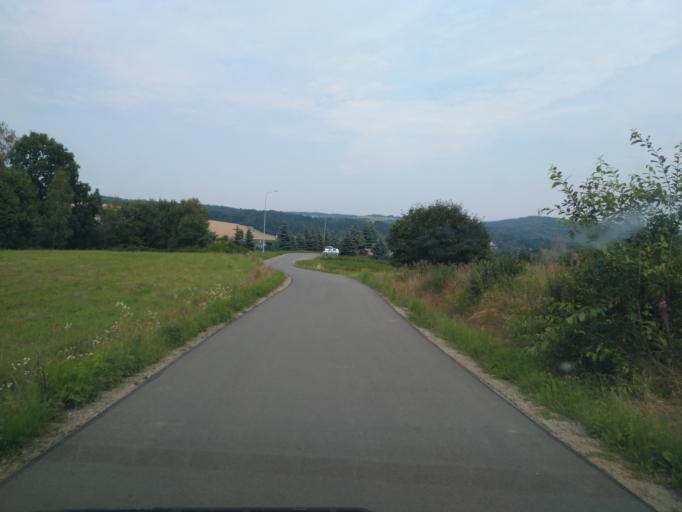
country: PL
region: Subcarpathian Voivodeship
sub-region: Powiat strzyzowski
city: Niebylec
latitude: 49.8549
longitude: 21.8966
